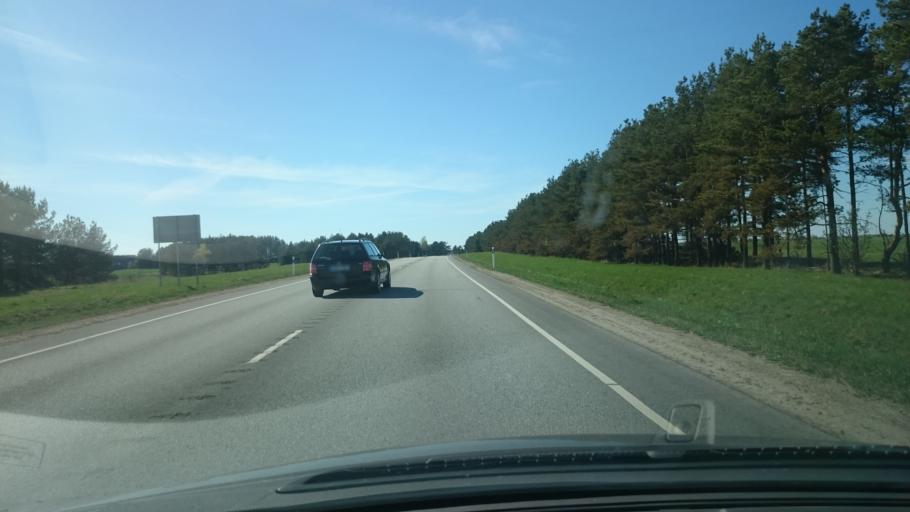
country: EE
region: Ida-Virumaa
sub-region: Puessi linn
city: Pussi
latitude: 59.4043
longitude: 27.0681
